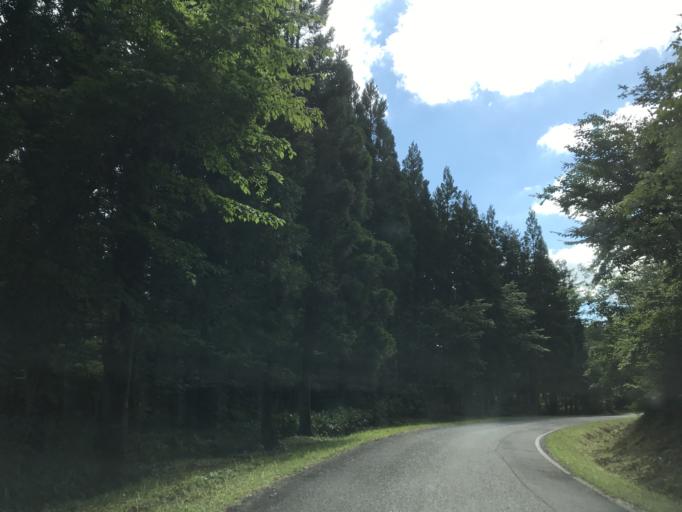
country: JP
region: Iwate
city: Ichinoseki
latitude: 38.9268
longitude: 140.9323
